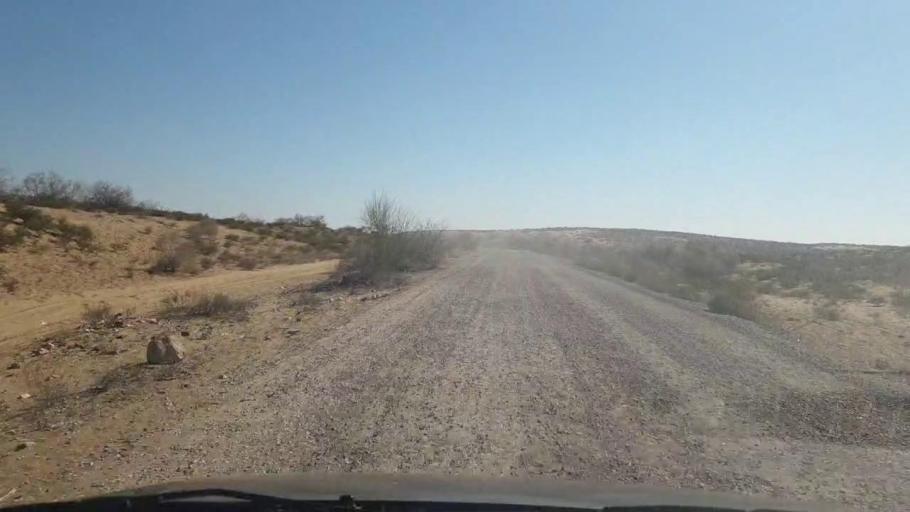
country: PK
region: Sindh
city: Bozdar
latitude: 27.0178
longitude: 68.7340
